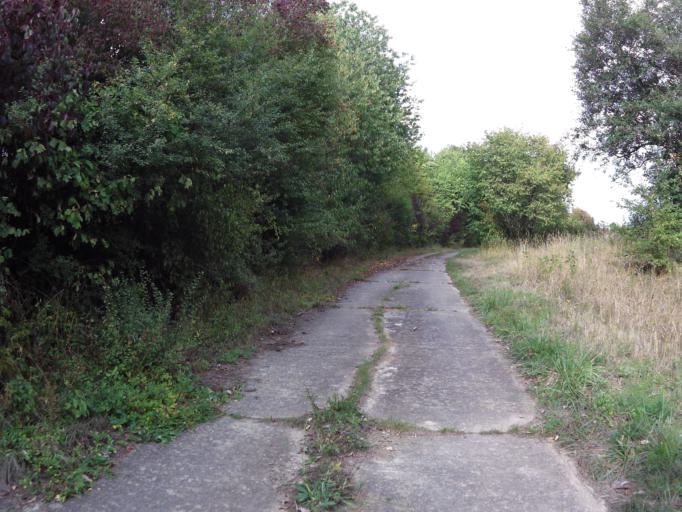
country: DE
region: Bavaria
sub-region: Regierungsbezirk Unterfranken
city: Eisingen
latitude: 49.7507
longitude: 9.8308
